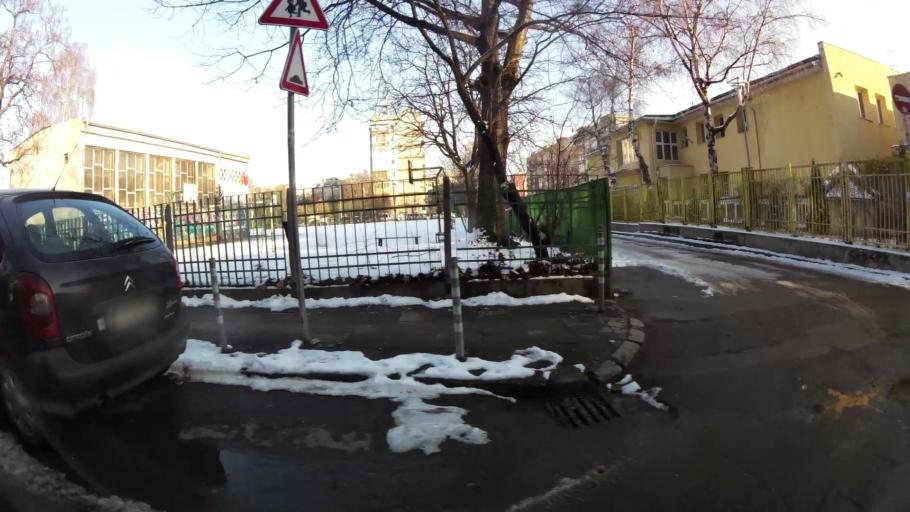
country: BG
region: Sofia-Capital
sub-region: Stolichna Obshtina
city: Sofia
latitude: 42.6821
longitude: 23.3615
